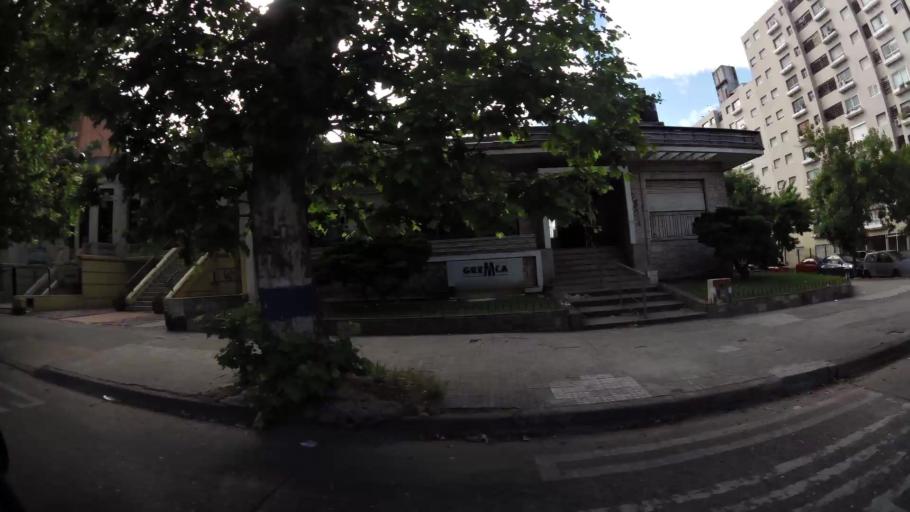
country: UY
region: Montevideo
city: Montevideo
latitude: -34.8870
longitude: -56.1582
